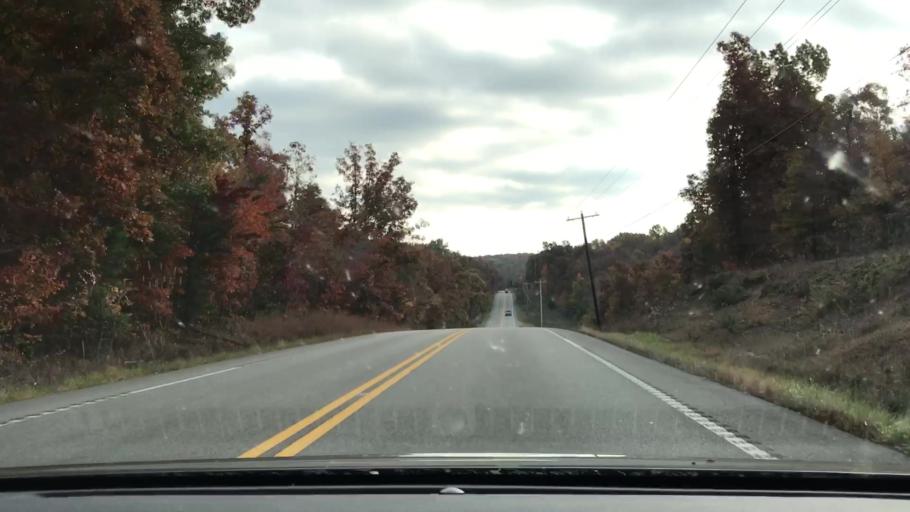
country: US
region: Tennessee
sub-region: Putnam County
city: Monterey
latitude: 36.1335
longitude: -85.2185
